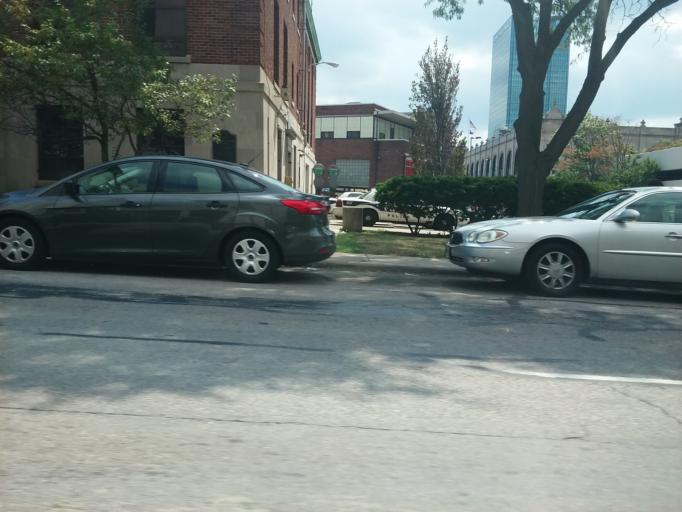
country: US
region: Ohio
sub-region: Lucas County
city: Toledo
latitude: 41.6567
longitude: -83.5349
